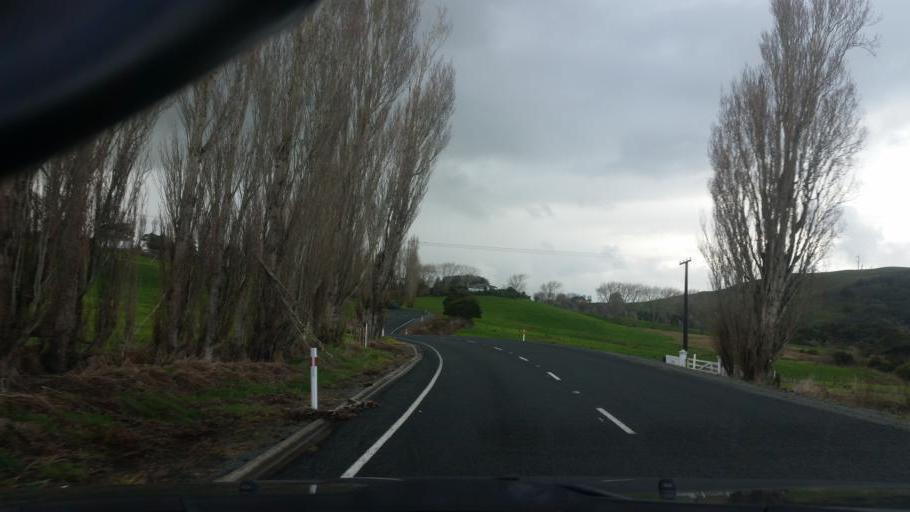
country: NZ
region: Northland
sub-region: Kaipara District
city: Dargaville
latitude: -36.1654
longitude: 174.1664
